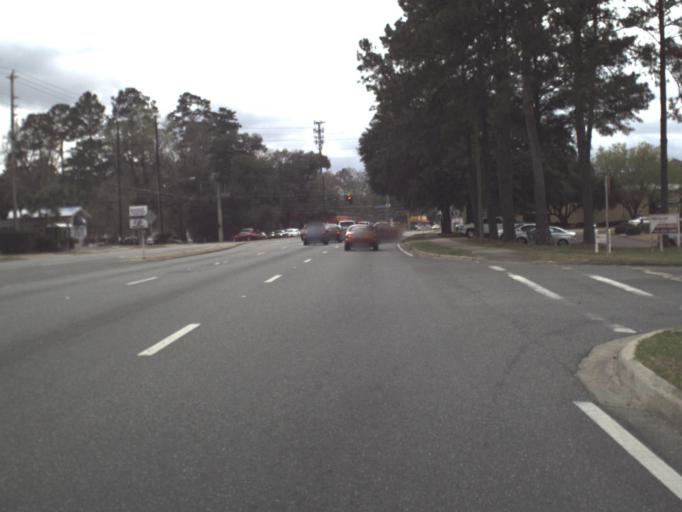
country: US
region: Florida
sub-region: Leon County
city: Tallahassee
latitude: 30.4678
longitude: -84.2679
